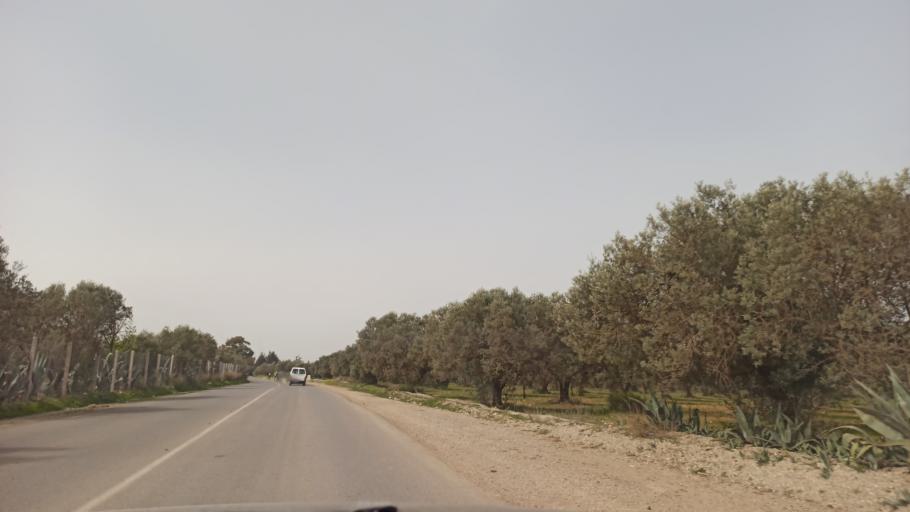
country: TN
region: Zaghwan
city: Zaghouan
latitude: 36.4189
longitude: 10.1134
